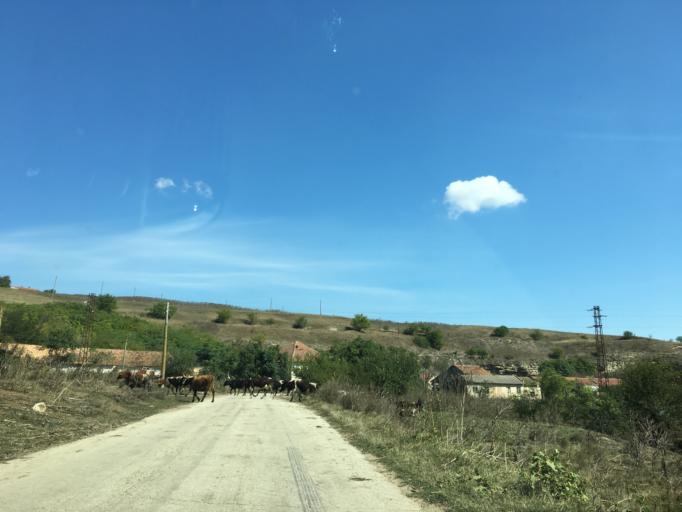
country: BG
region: Pleven
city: Iskur
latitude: 43.5653
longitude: 24.2095
